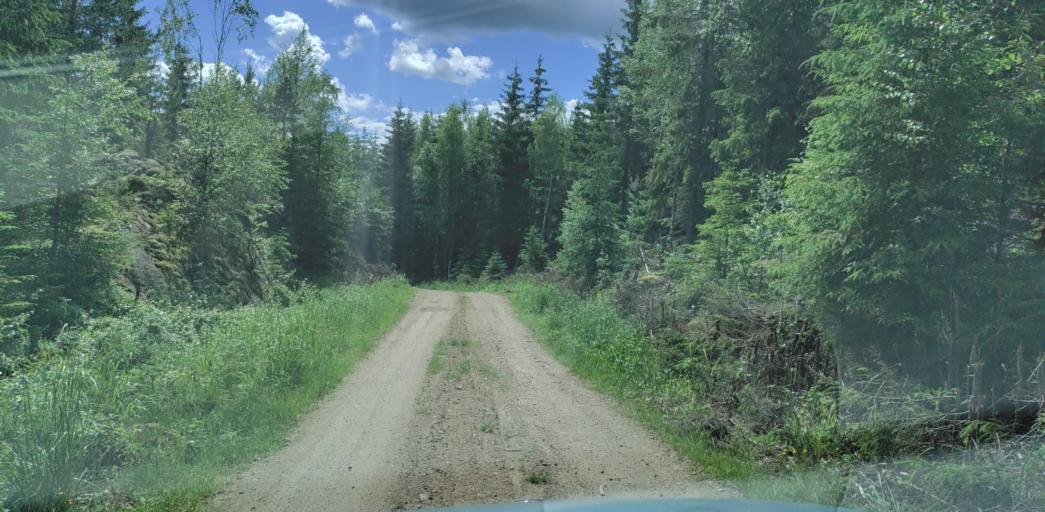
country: SE
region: Vaermland
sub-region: Hagfors Kommun
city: Ekshaerad
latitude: 60.1110
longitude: 13.3249
